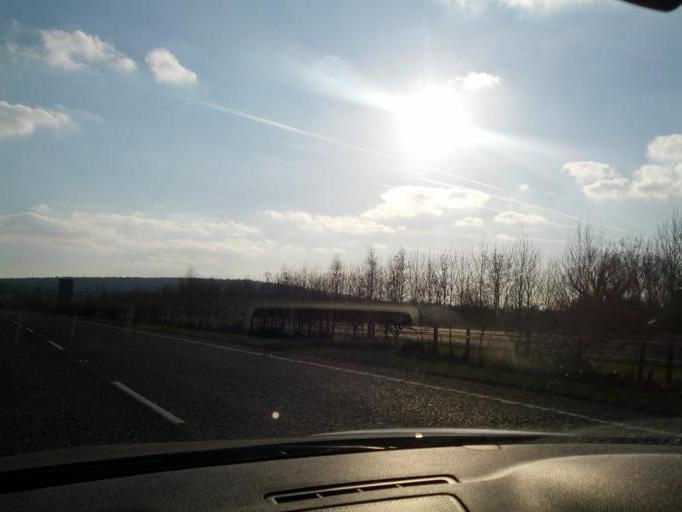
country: IE
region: Leinster
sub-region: Kildare
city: Monasterevin
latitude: 53.1382
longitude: -7.0326
